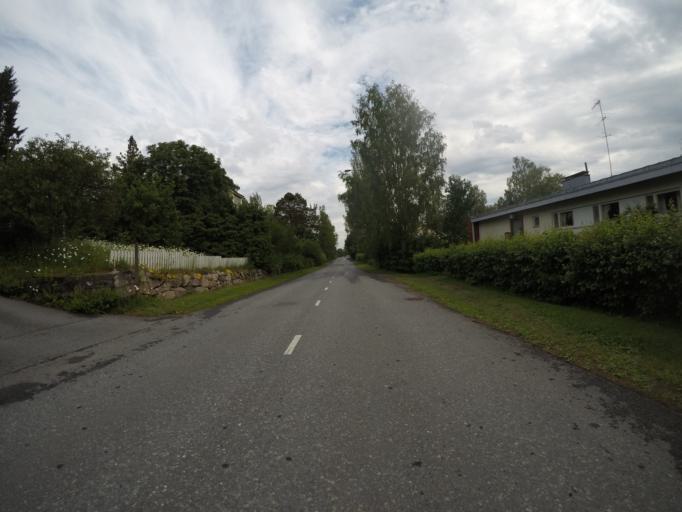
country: FI
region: Haeme
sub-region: Haemeenlinna
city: Haemeenlinna
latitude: 61.0076
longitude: 24.4858
